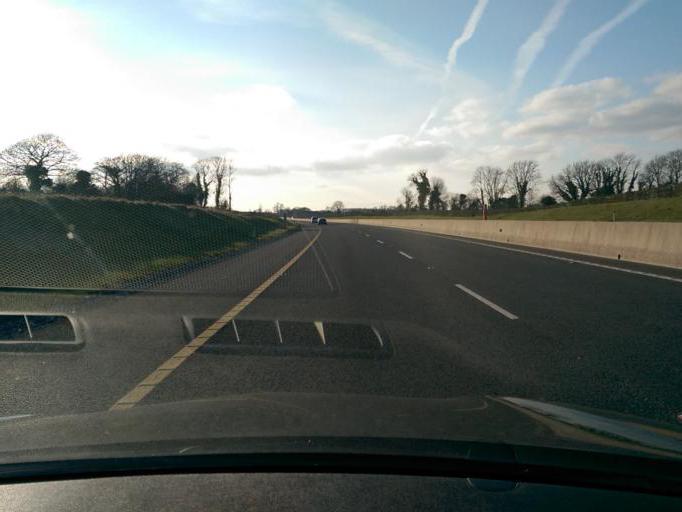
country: IE
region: Leinster
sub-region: Laois
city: Rathdowney
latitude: 52.9181
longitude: -7.5484
